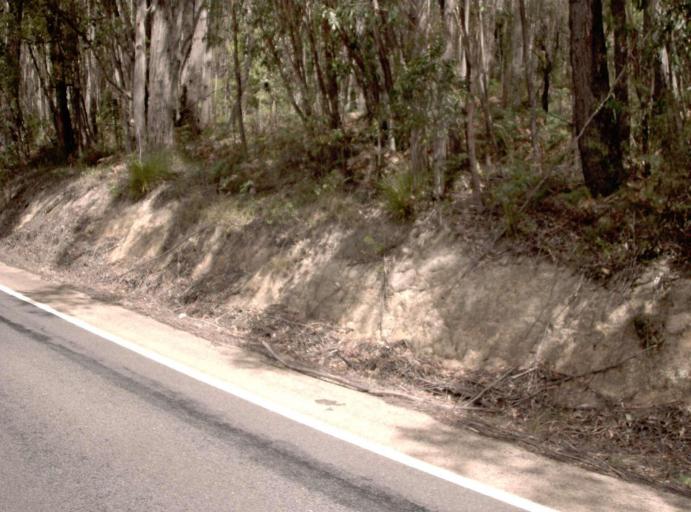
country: AU
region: New South Wales
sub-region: Bombala
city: Bombala
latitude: -37.5363
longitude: 149.3931
